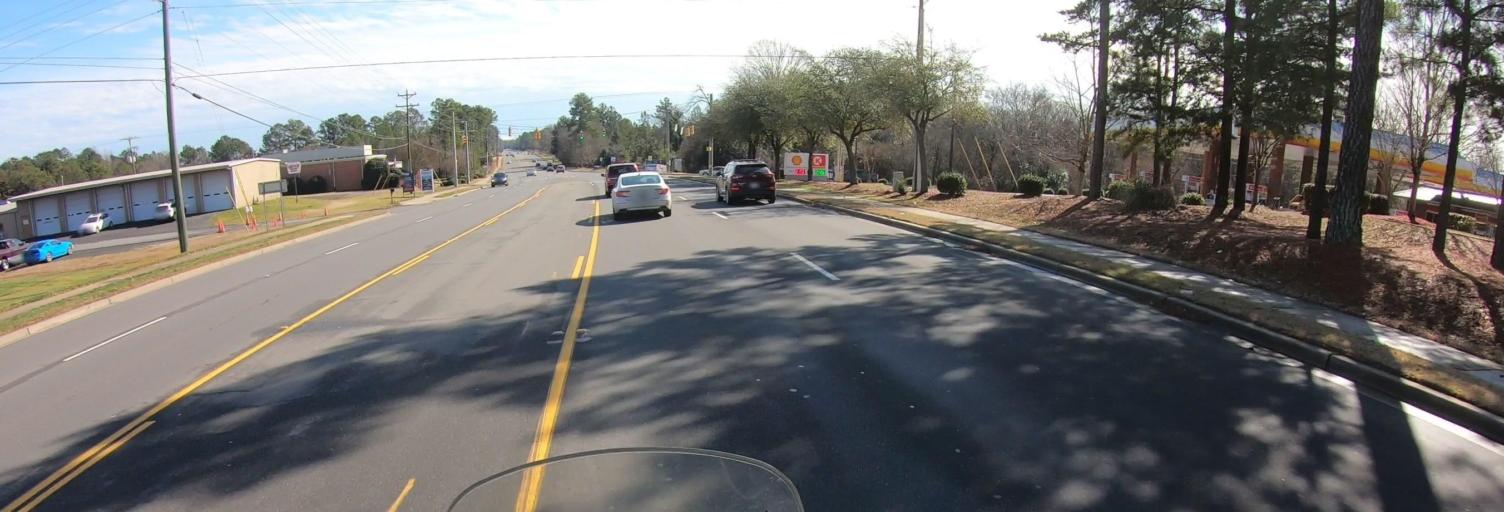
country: US
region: South Carolina
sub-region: York County
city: Tega Cay
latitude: 35.0467
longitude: -80.9898
